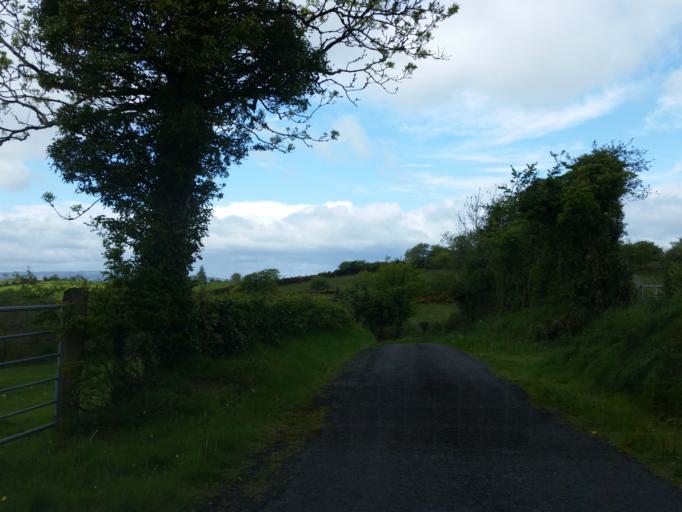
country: GB
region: Northern Ireland
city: Lisnaskea
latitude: 54.2655
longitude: -7.3921
